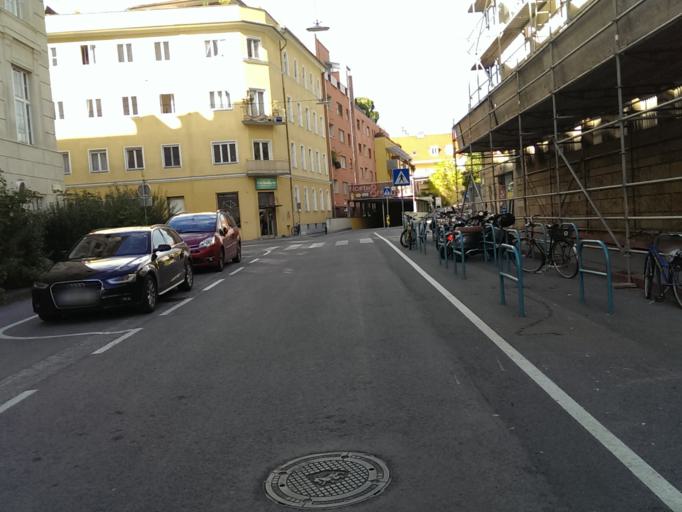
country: AT
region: Styria
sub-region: Graz Stadt
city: Graz
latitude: 47.0648
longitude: 15.4516
